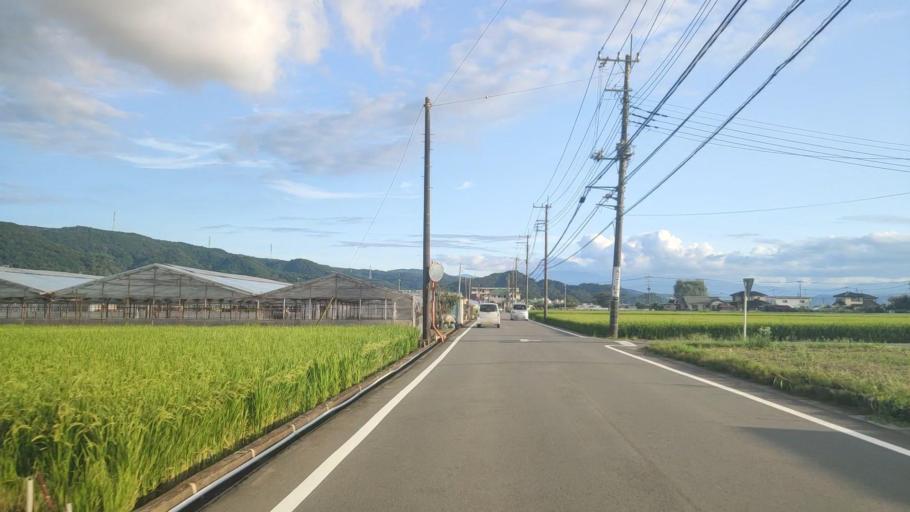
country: JP
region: Shizuoka
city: Mishima
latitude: 35.0687
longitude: 138.9517
